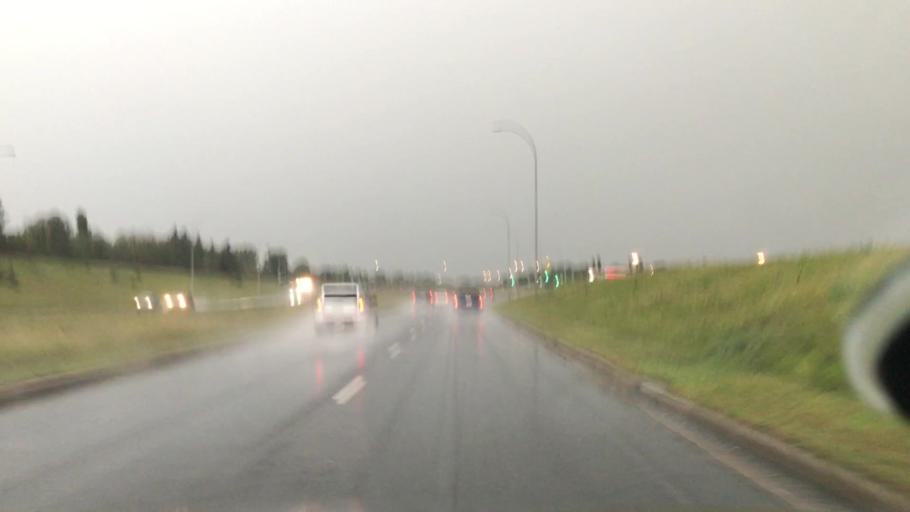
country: CA
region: Alberta
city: Edmonton
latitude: 53.4731
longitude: -113.5776
